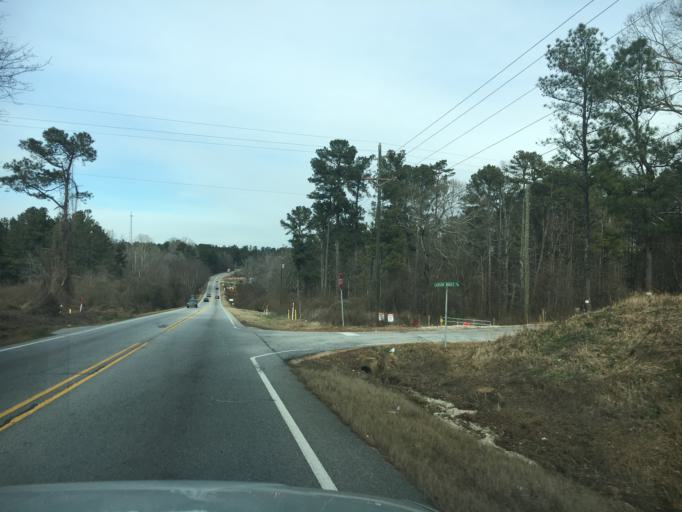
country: US
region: Georgia
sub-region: Barrow County
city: Winder
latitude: 33.9577
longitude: -83.7475
